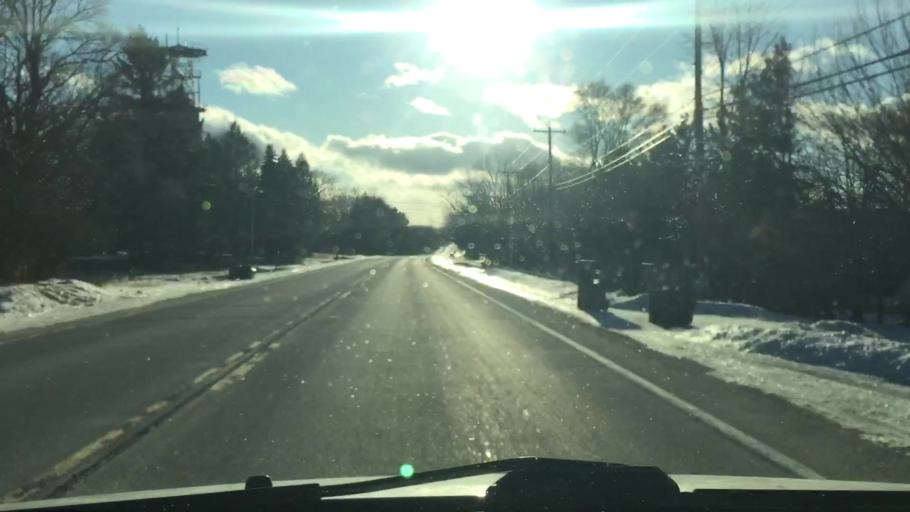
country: US
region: Wisconsin
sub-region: Waukesha County
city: Muskego
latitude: 42.9415
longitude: -88.1645
